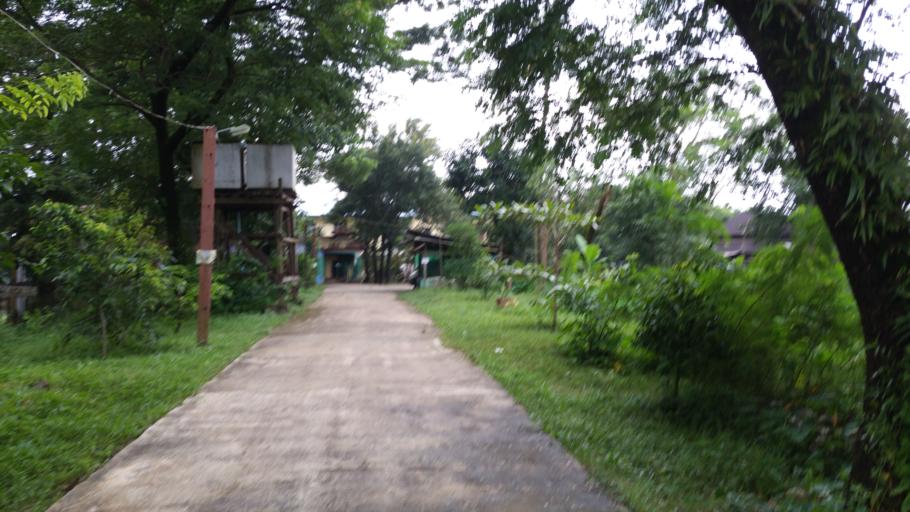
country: MM
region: Yangon
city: Yangon
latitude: 16.7634
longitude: 96.1486
